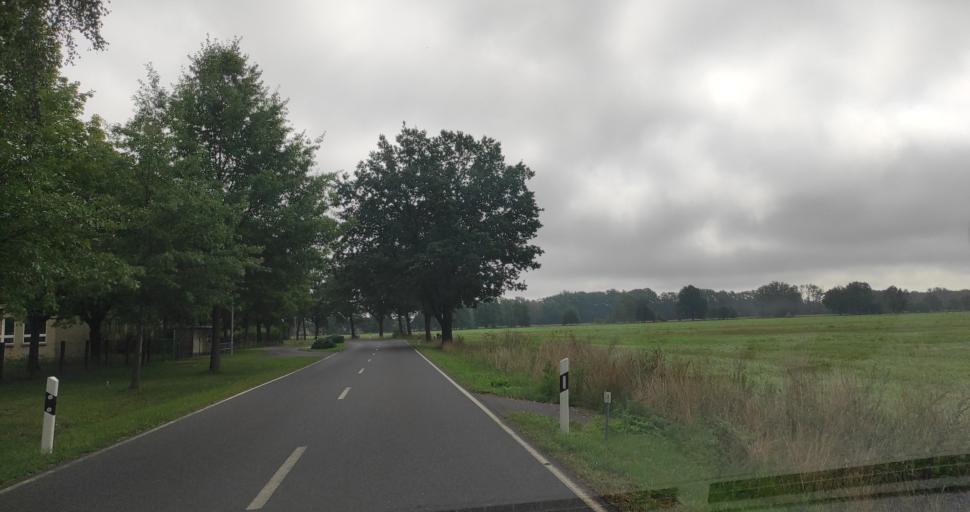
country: DE
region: Brandenburg
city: Forst
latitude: 51.6881
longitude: 14.6223
